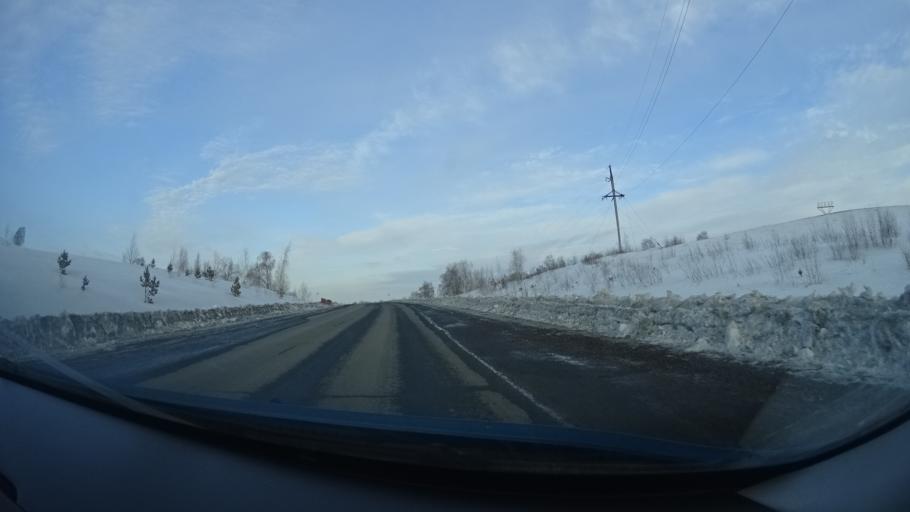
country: RU
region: Bashkortostan
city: Tubinskiy
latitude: 53.3166
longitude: 58.4945
